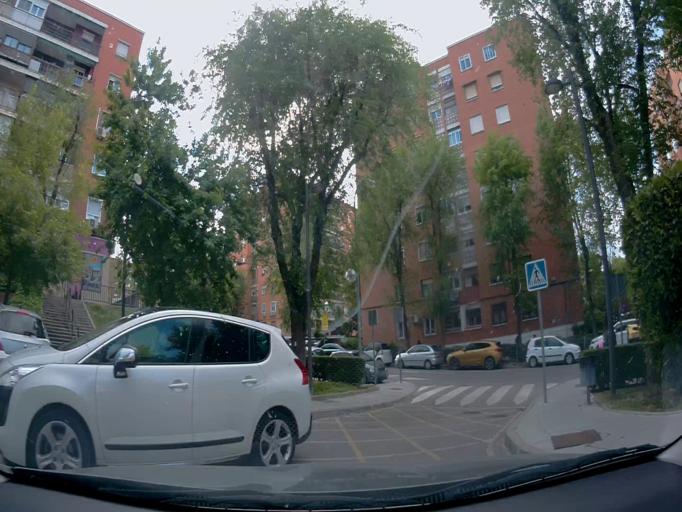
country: ES
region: Madrid
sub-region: Provincia de Madrid
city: Mostoles
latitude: 40.3161
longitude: -3.8755
